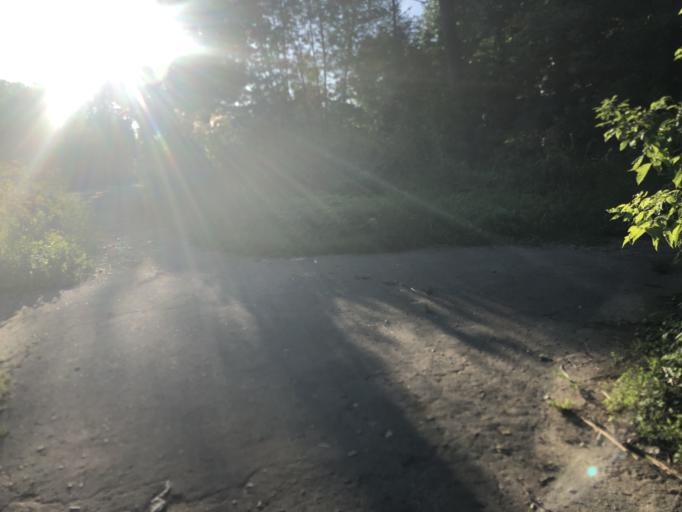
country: RU
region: Tverskaya
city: Rzhev
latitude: 56.2438
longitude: 34.3266
